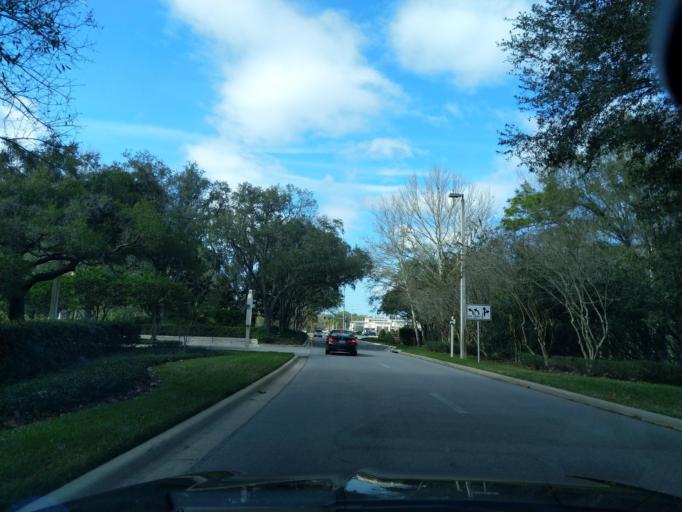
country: US
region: Florida
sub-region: Hillsborough County
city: Pebble Creek
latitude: 28.1371
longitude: -82.3569
